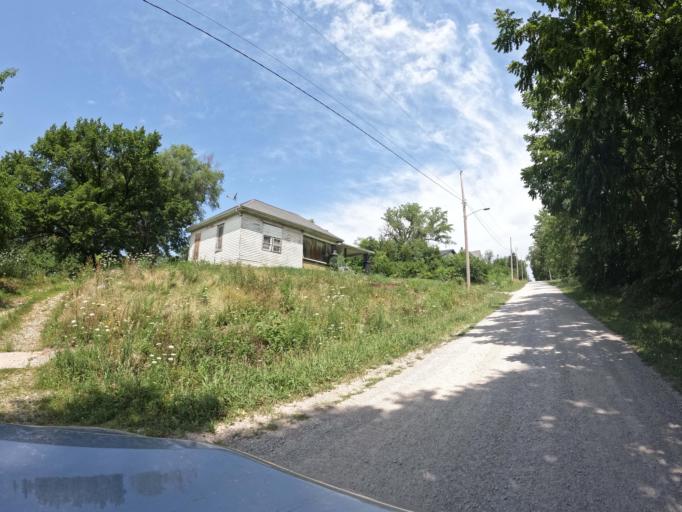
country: US
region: Iowa
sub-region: Appanoose County
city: Centerville
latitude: 40.7783
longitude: -92.9454
